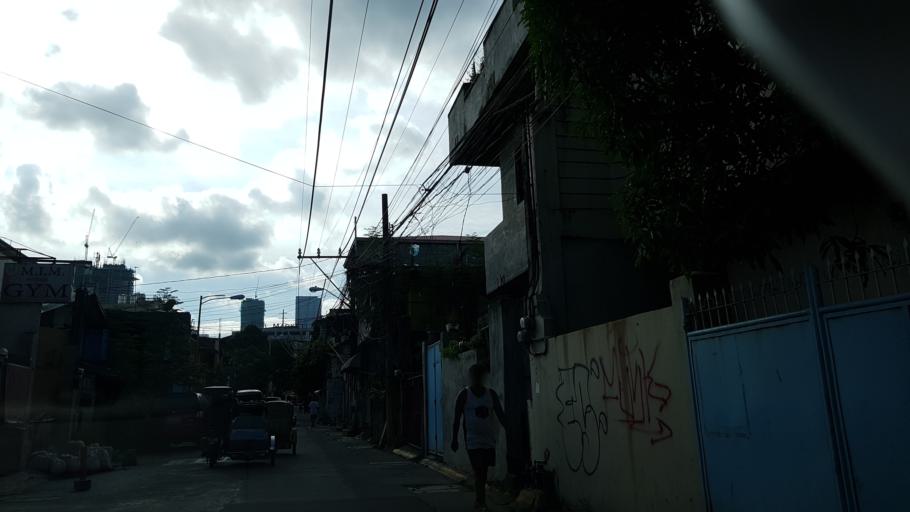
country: PH
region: Calabarzon
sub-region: Province of Rizal
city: Pateros
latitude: 14.5481
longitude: 121.0608
